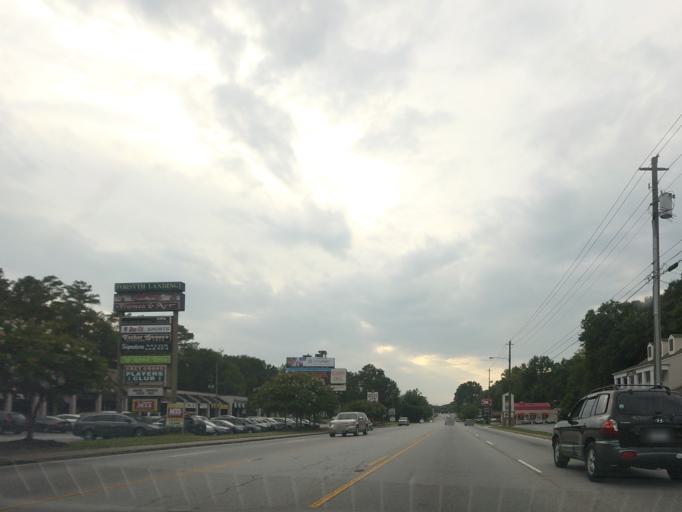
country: US
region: Georgia
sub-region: Bibb County
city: Macon
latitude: 32.8717
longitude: -83.7043
